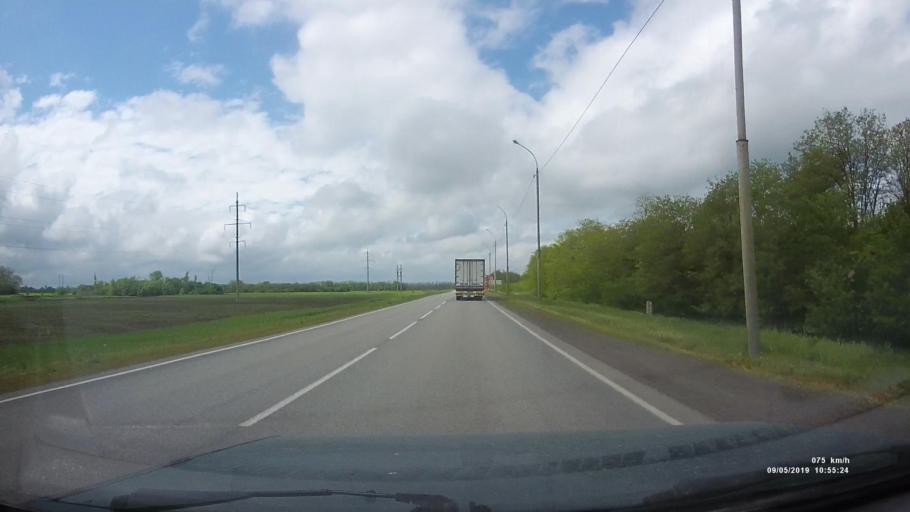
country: RU
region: Rostov
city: Peshkovo
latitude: 46.8727
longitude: 39.3160
